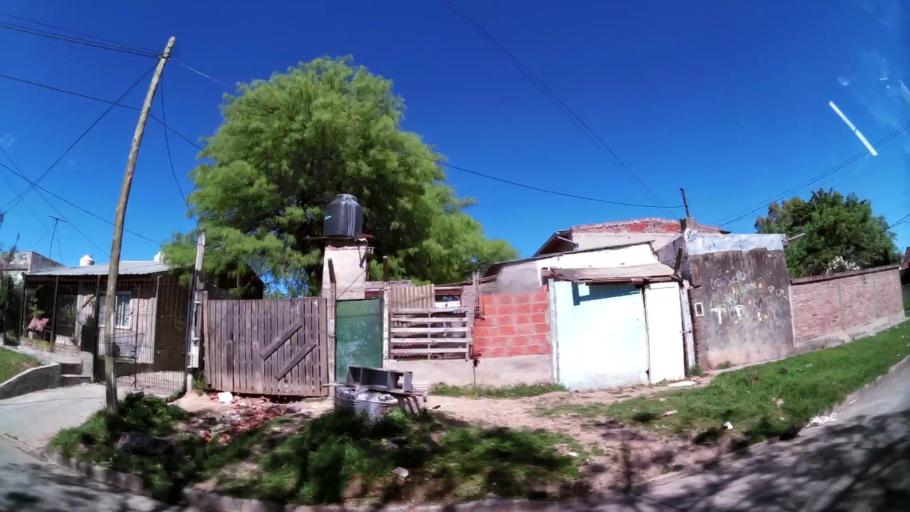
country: AR
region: Buenos Aires
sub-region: Partido de Tigre
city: Tigre
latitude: -34.4995
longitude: -58.6116
